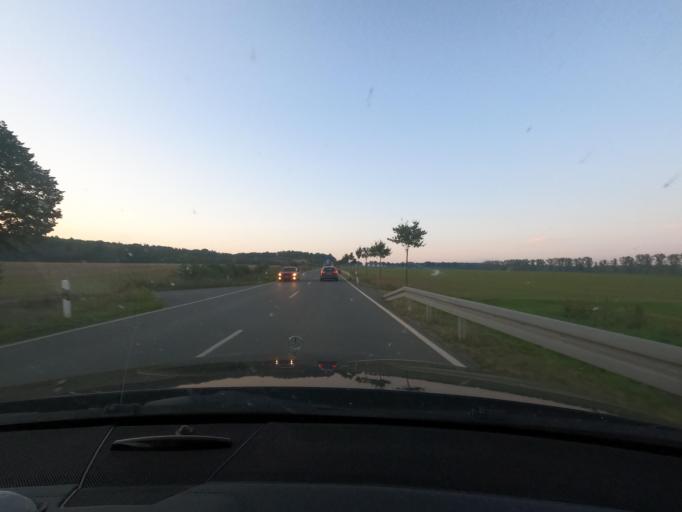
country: DE
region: North Rhine-Westphalia
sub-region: Regierungsbezirk Detmold
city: Salzkotten
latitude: 51.6265
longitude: 8.5863
